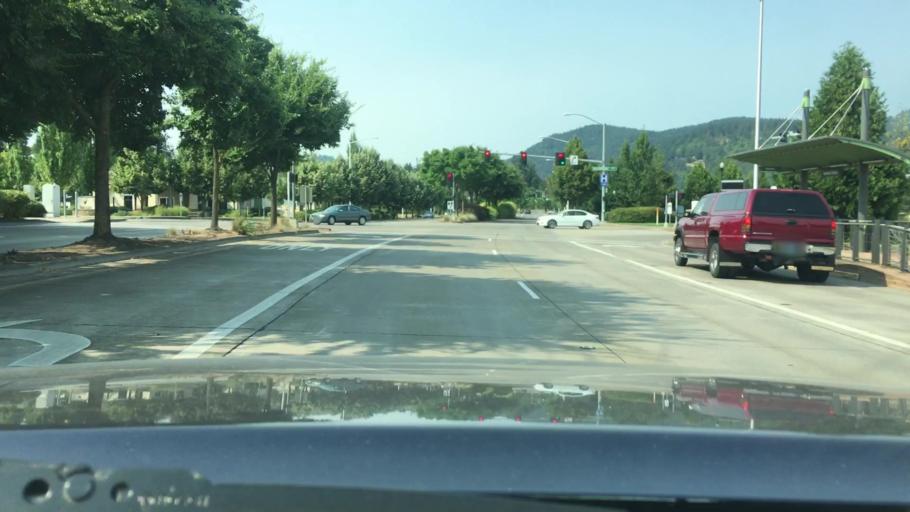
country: US
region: Oregon
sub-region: Lane County
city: Springfield
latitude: 44.0774
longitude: -123.0311
